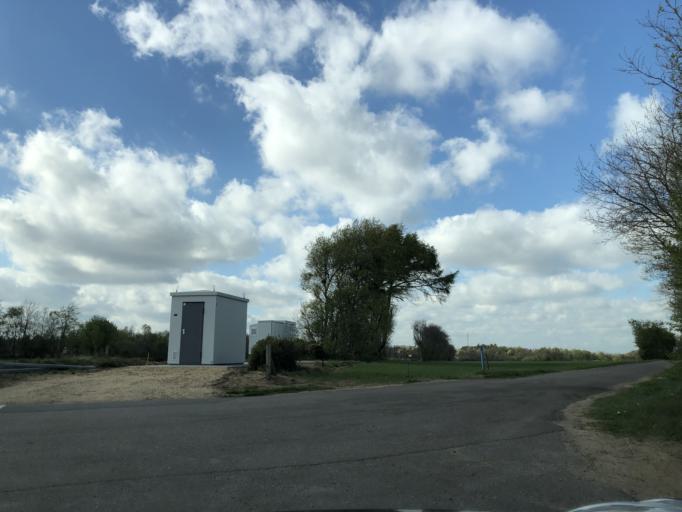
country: DK
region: Central Jutland
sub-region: Herning Kommune
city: Avlum
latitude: 56.2973
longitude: 8.7409
